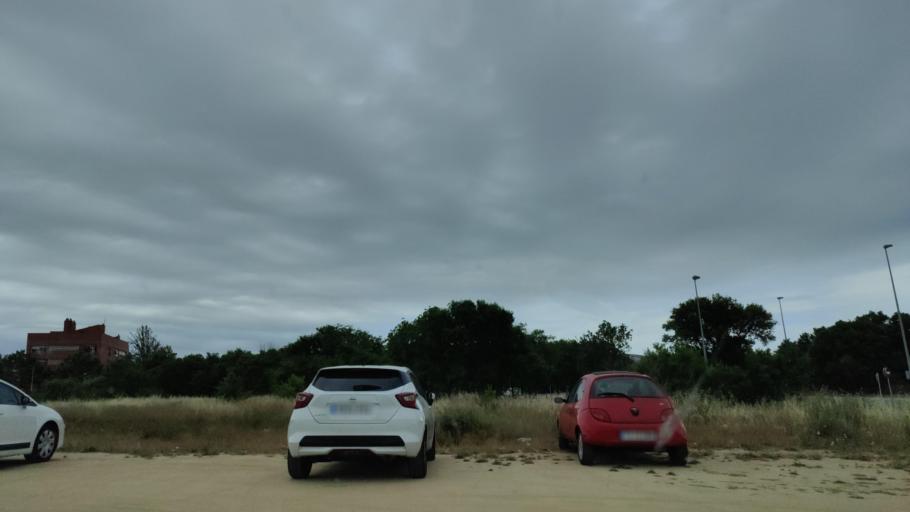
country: ES
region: Catalonia
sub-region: Provincia de Barcelona
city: El Prat de Llobregat
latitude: 41.3141
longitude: 2.0832
